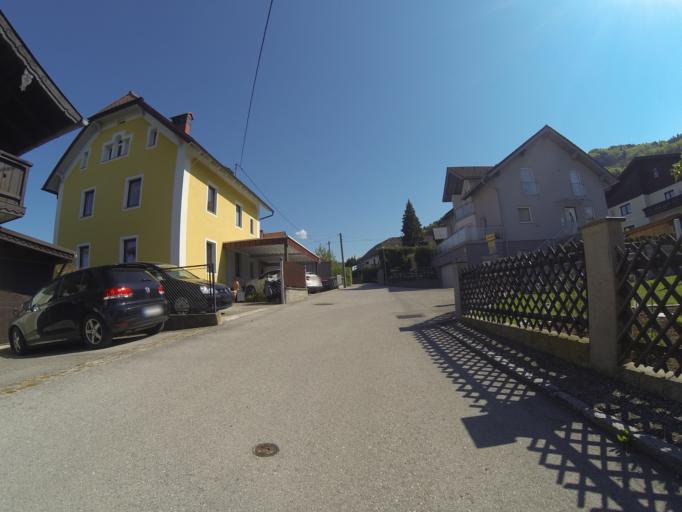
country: AT
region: Upper Austria
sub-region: Politischer Bezirk Gmunden
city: Altmunster
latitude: 47.9303
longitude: 13.7674
